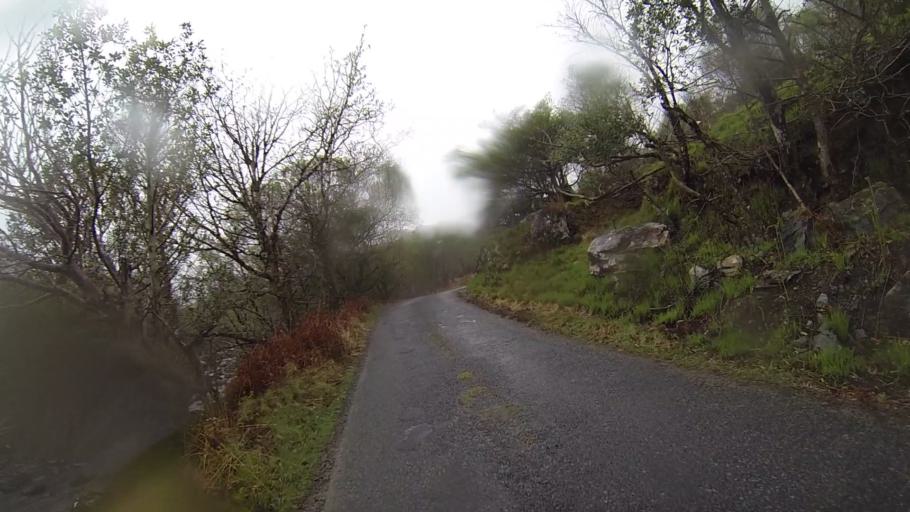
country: IE
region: Munster
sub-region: Ciarrai
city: Kenmare
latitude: 51.9639
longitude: -9.6358
